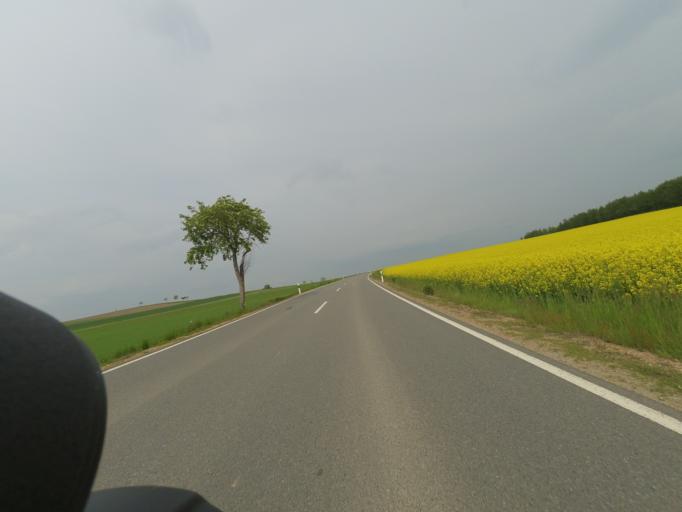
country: DE
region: Saxony
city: Lichtenberg
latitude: 50.8406
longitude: 13.4422
